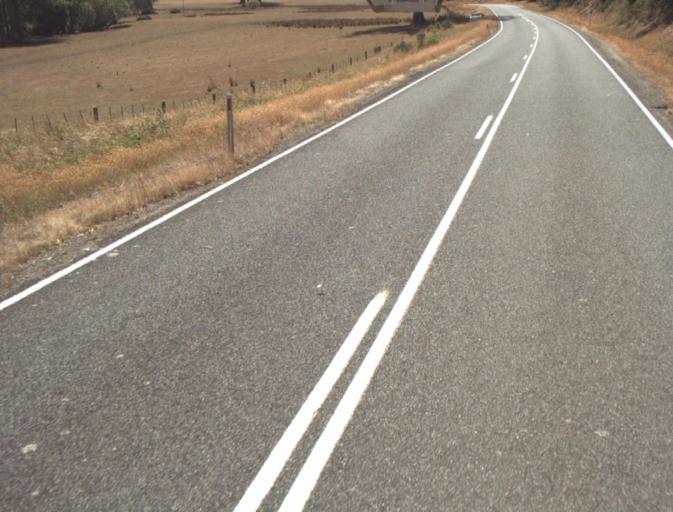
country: AU
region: Tasmania
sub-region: Dorset
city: Scottsdale
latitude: -41.2987
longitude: 147.3840
